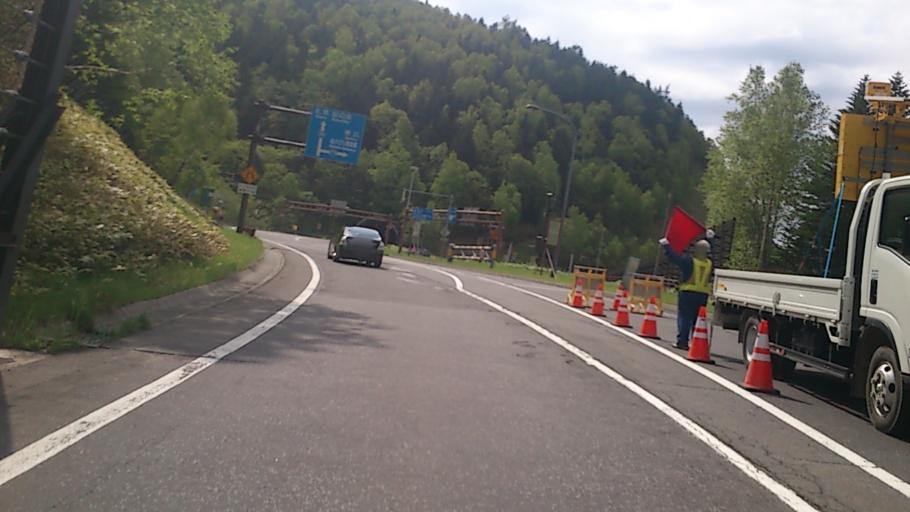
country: JP
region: Hokkaido
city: Kamikawa
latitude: 43.6815
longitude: 143.0358
